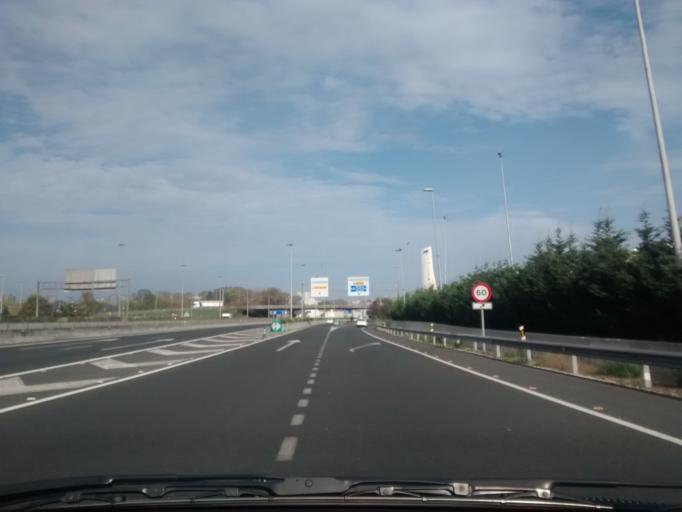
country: ES
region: Cantabria
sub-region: Provincia de Cantabria
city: El Astillero
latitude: 43.4376
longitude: -3.8371
